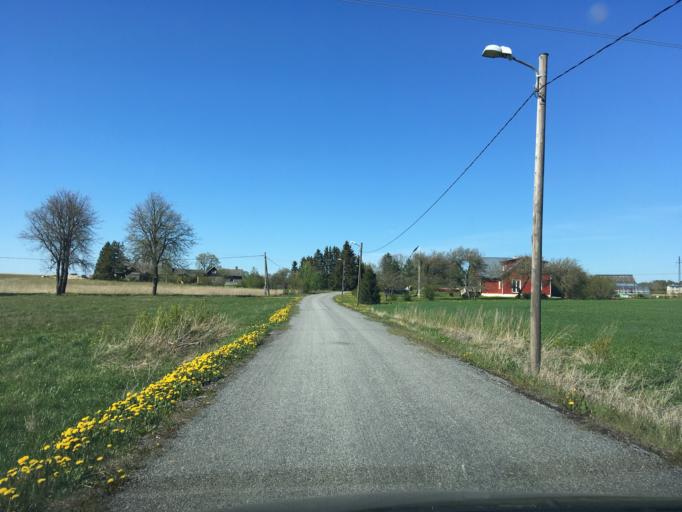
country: EE
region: Harju
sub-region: Raasiku vald
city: Arukula
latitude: 59.2688
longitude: 25.0944
